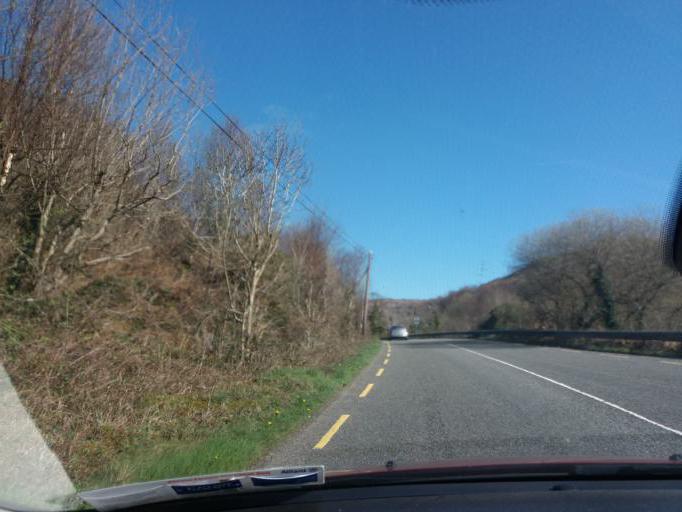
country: IE
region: Munster
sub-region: Ciarrai
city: Cill Airne
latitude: 51.9230
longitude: -9.3846
